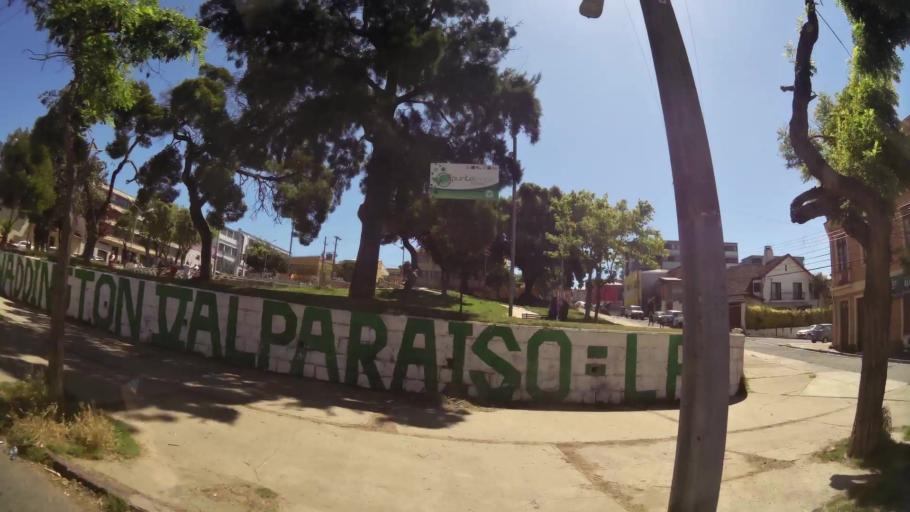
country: CL
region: Valparaiso
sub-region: Provincia de Valparaiso
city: Valparaiso
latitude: -33.0288
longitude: -71.6333
